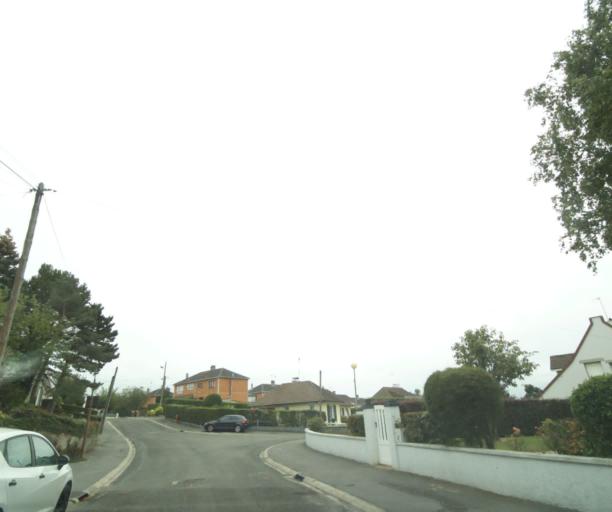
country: FR
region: Nord-Pas-de-Calais
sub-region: Departement du Pas-de-Calais
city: Etaples
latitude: 50.5242
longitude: 1.6370
